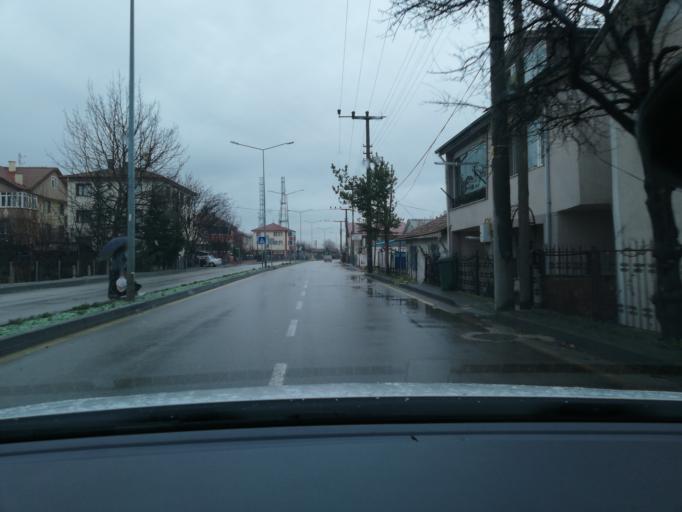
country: TR
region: Bolu
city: Bolu
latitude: 40.7232
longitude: 31.6140
